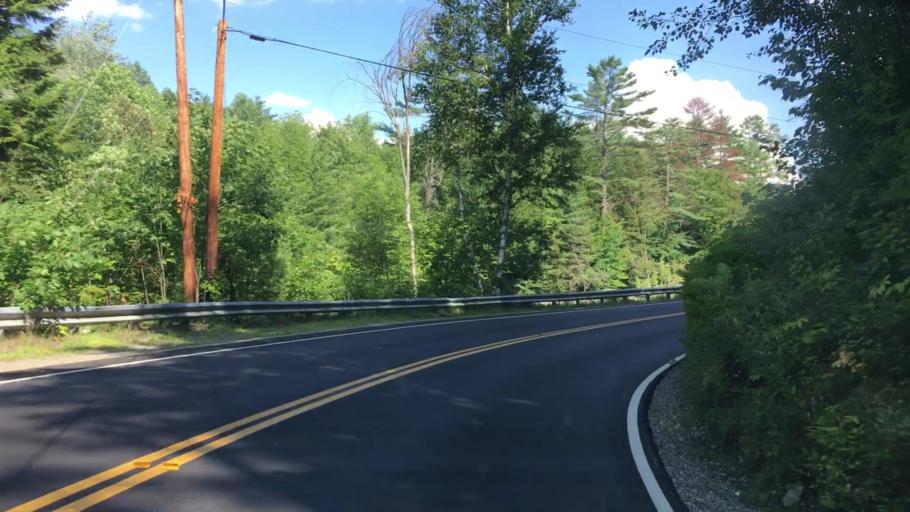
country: US
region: New Hampshire
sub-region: Grafton County
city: North Haverhill
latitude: 44.1212
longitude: -71.9228
